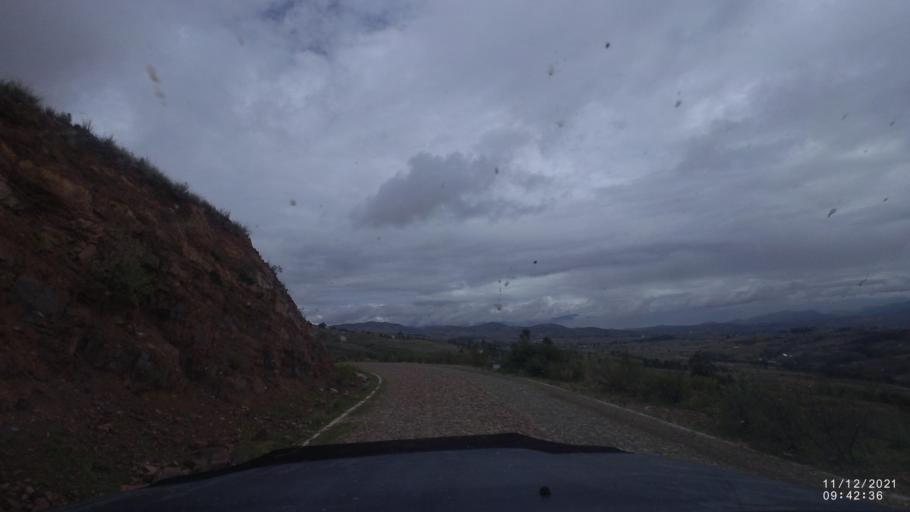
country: BO
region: Cochabamba
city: Tarata
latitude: -17.8088
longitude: -65.9757
